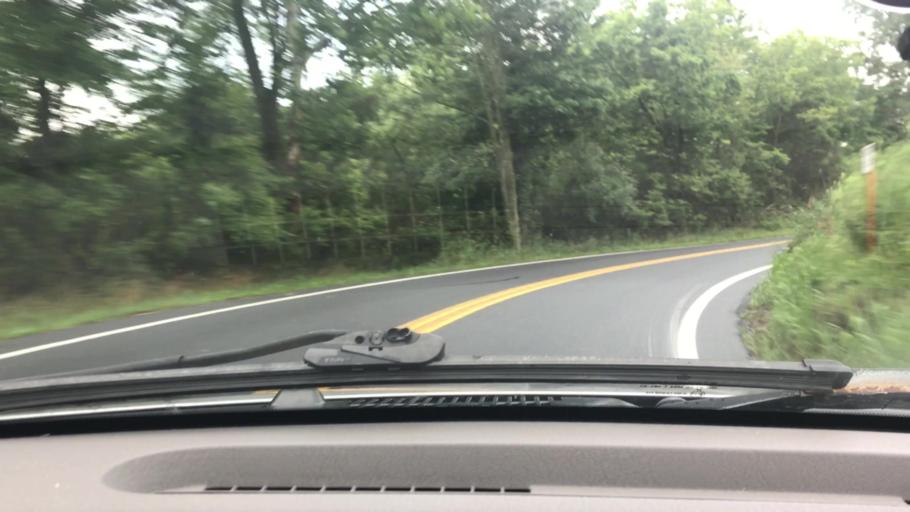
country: US
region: Pennsylvania
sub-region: Lancaster County
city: Elizabethtown
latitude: 40.2028
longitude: -76.6387
